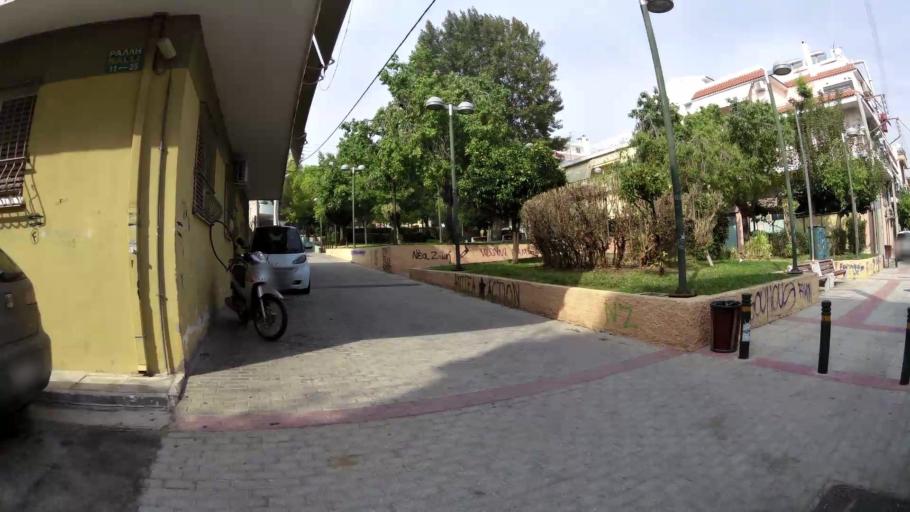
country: GR
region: Attica
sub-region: Nomarchia Athinas
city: Chaidari
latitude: 38.0184
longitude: 23.6755
